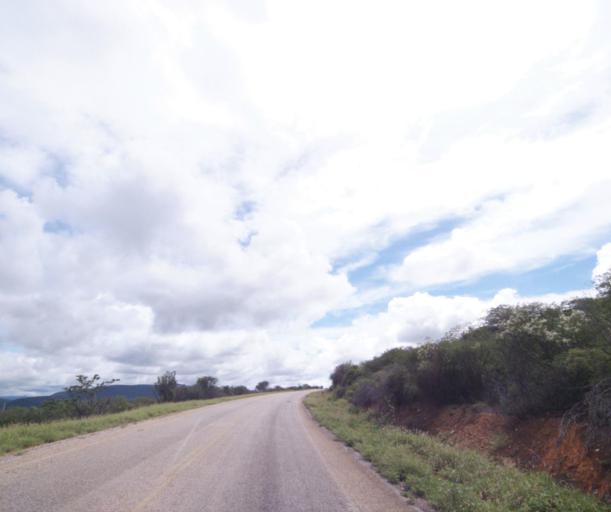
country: BR
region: Bahia
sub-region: Brumado
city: Brumado
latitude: -14.2004
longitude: -41.6169
